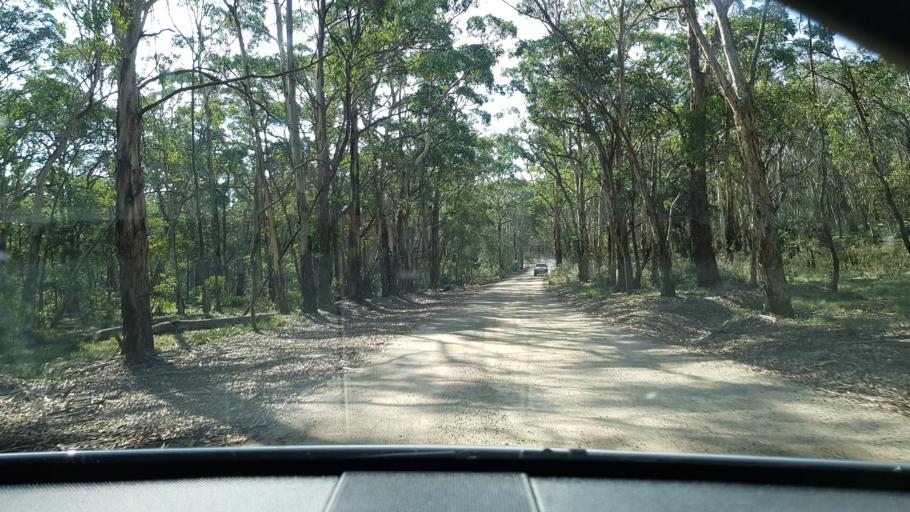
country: AU
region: New South Wales
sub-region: Oberon
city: Oberon
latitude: -33.9825
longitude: 150.0595
